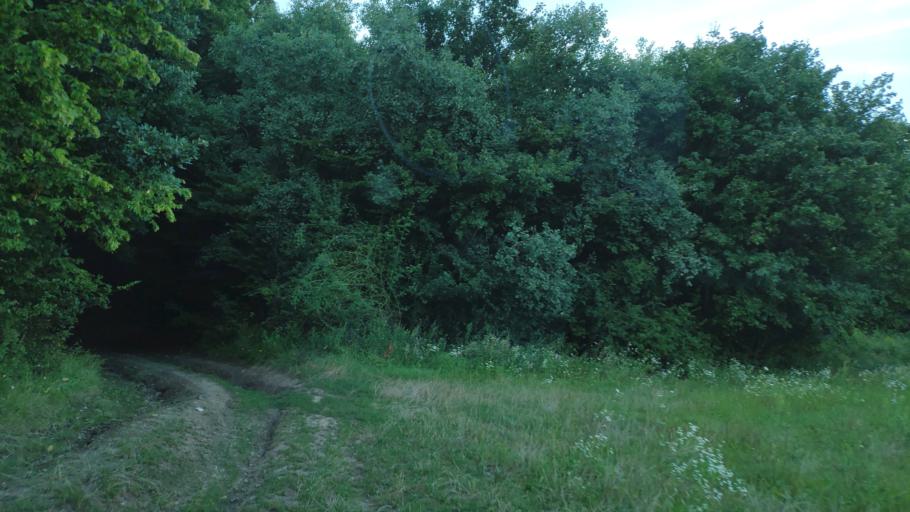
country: SK
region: Kosicky
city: Secovce
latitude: 48.5924
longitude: 21.5342
